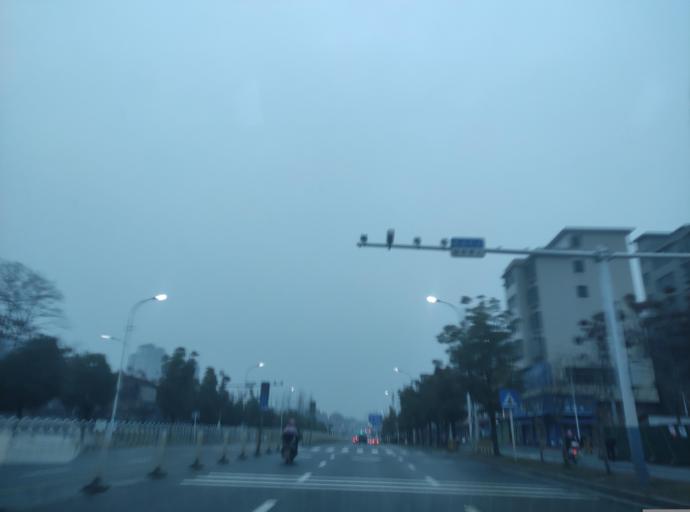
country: CN
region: Jiangxi Sheng
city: Pingxiang
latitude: 27.6686
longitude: 113.8674
